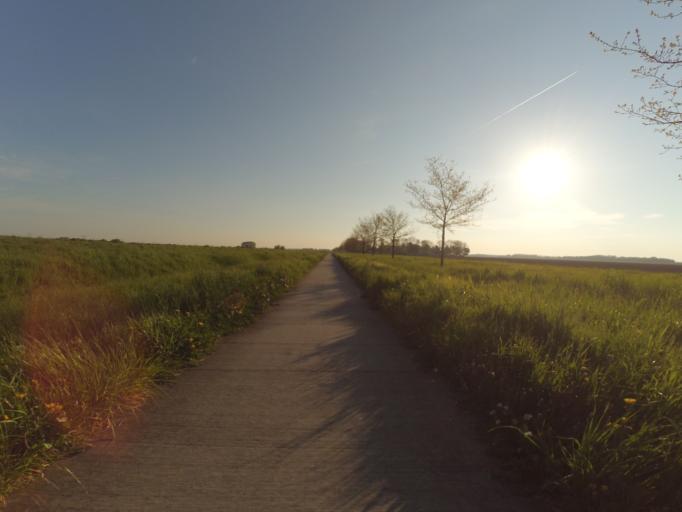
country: NL
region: Flevoland
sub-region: Gemeente Lelystad
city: Lelystad
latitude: 52.4484
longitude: 5.4694
